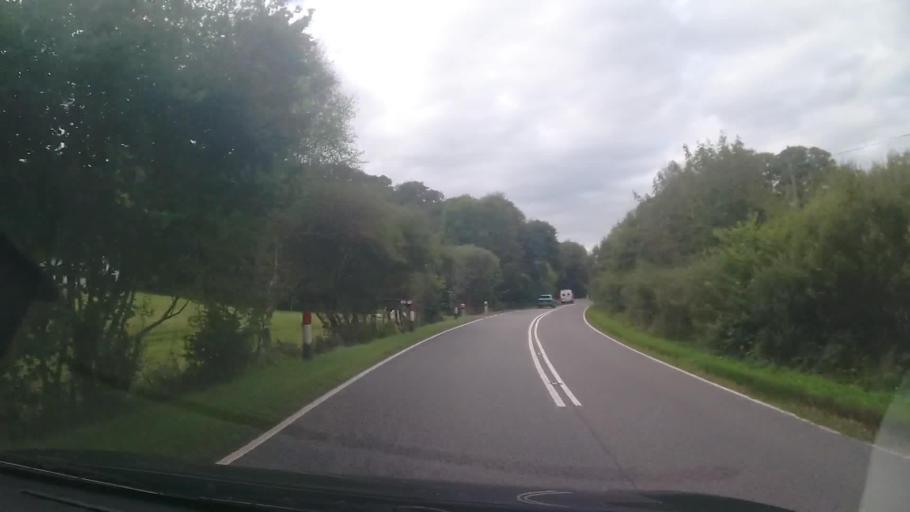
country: GB
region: Scotland
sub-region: Highland
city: Fort William
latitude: 56.6358
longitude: -5.2932
